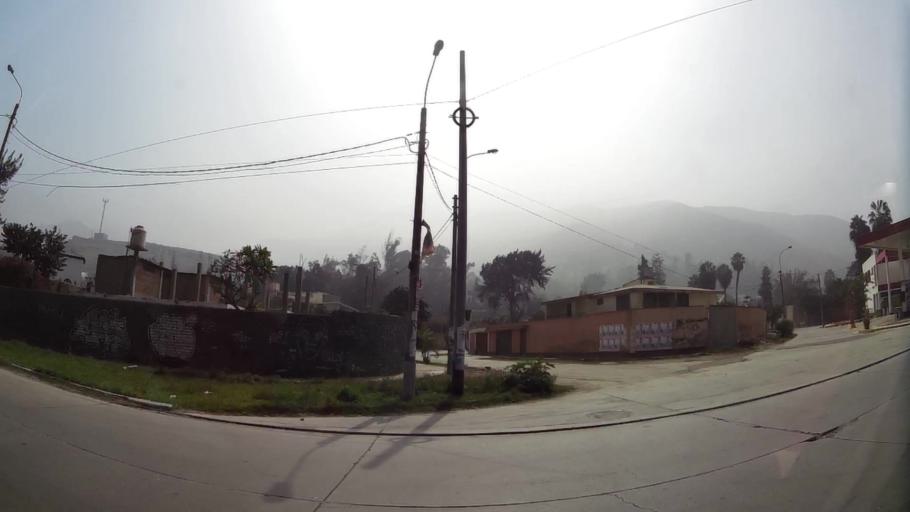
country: PE
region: Lima
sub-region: Lima
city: Chosica
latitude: -11.9503
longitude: -76.7241
